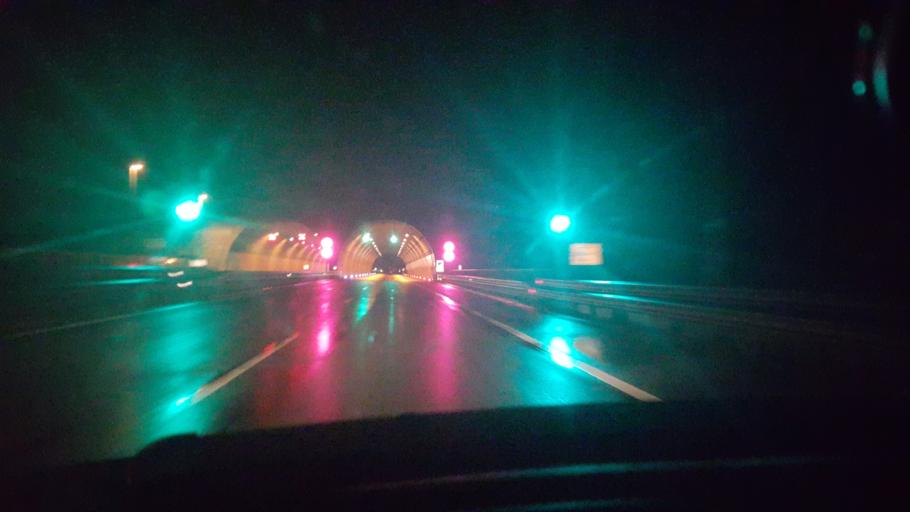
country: SI
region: Maribor
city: Maribor
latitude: 46.5596
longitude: 15.6871
